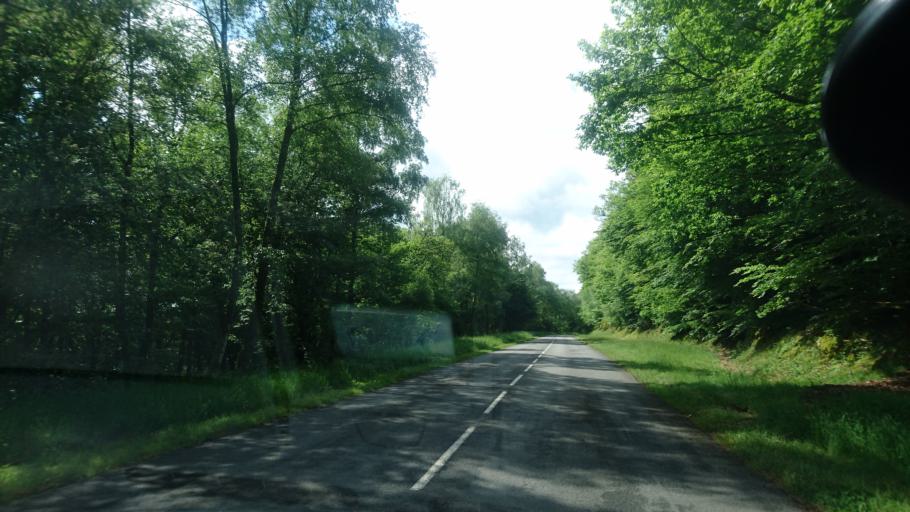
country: FR
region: Limousin
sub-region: Departement de la Haute-Vienne
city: Peyrat-le-Chateau
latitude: 45.7925
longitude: 1.8509
